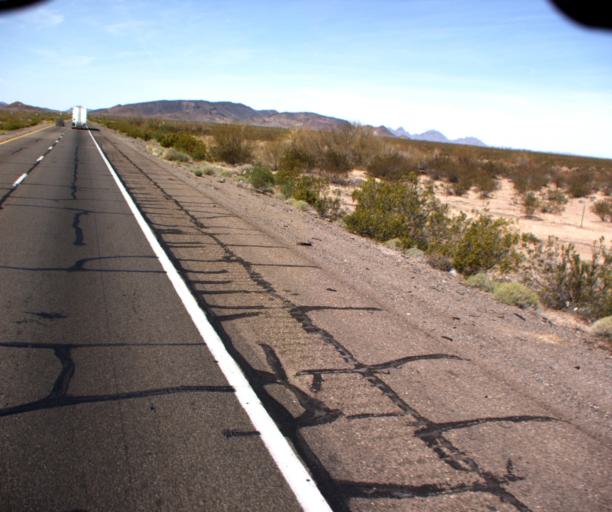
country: US
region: Arizona
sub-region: La Paz County
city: Salome
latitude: 33.6403
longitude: -113.8308
